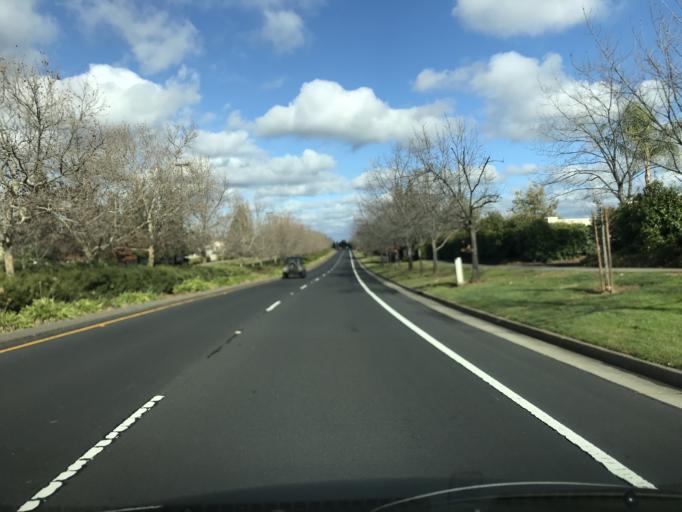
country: US
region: California
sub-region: Sacramento County
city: Folsom
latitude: 38.6547
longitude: -121.1402
